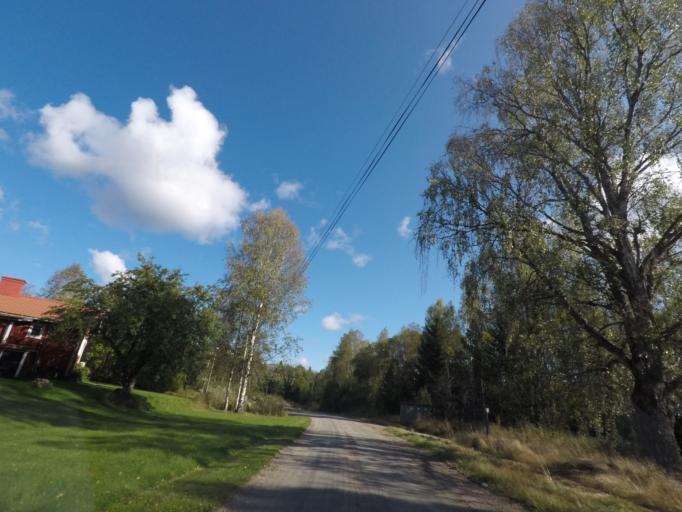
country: SE
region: Vaestmanland
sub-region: Skinnskattebergs Kommun
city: Skinnskatteberg
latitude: 59.8258
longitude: 15.5203
